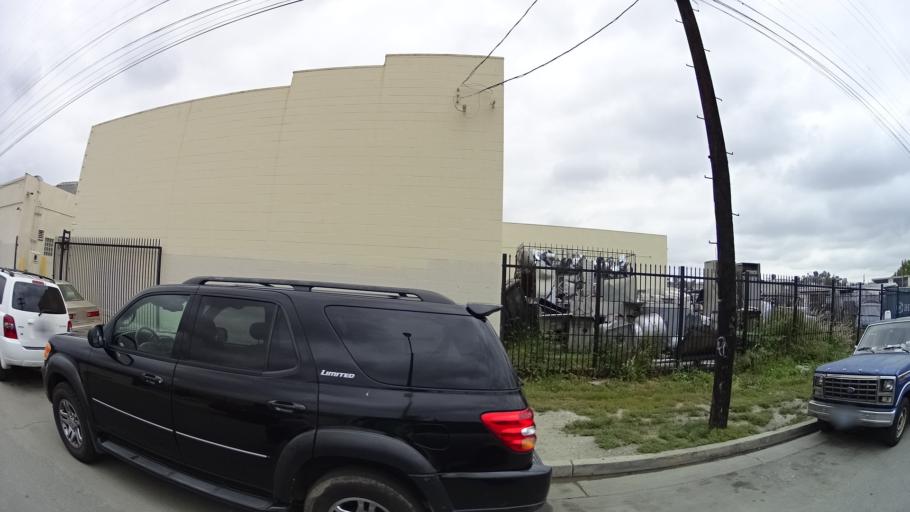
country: US
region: California
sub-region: Los Angeles County
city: Boyle Heights
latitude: 34.0613
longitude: -118.1933
